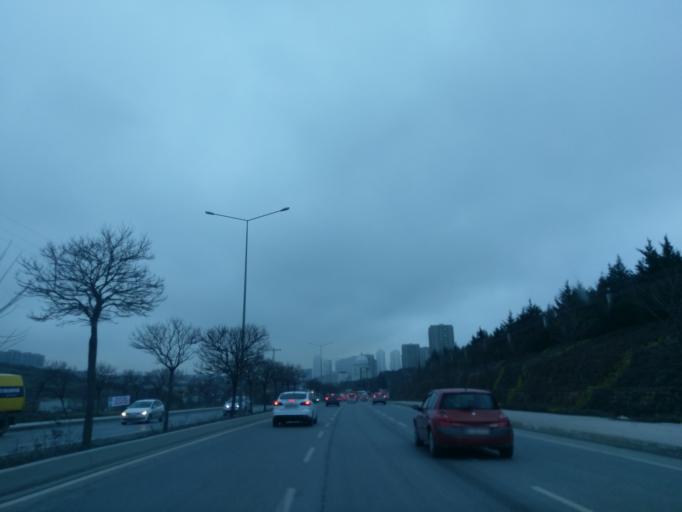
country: TR
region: Istanbul
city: Mahmutbey
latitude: 41.0445
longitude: 28.7739
